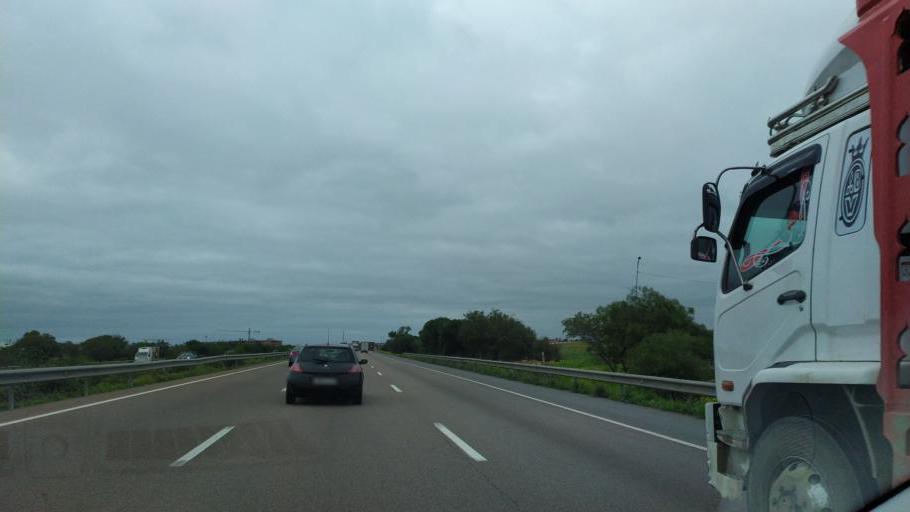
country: MA
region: Grand Casablanca
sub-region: Mohammedia
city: Mohammedia
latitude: 33.7377
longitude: -7.3036
